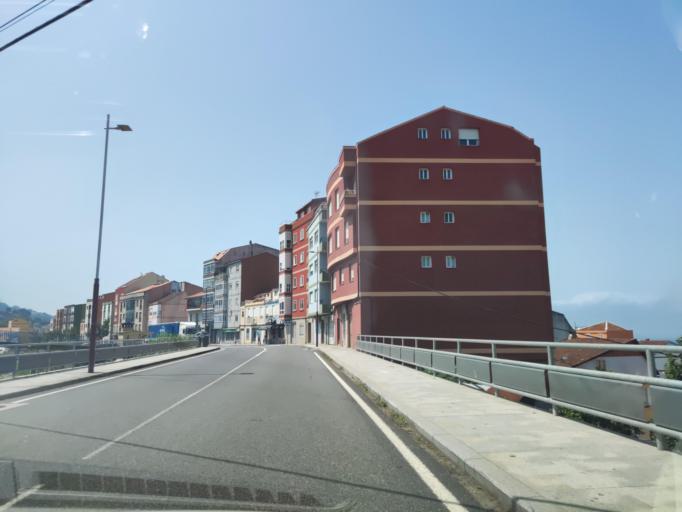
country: ES
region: Galicia
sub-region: Provincia de Pontevedra
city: Redondela
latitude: 42.2706
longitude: -8.6691
